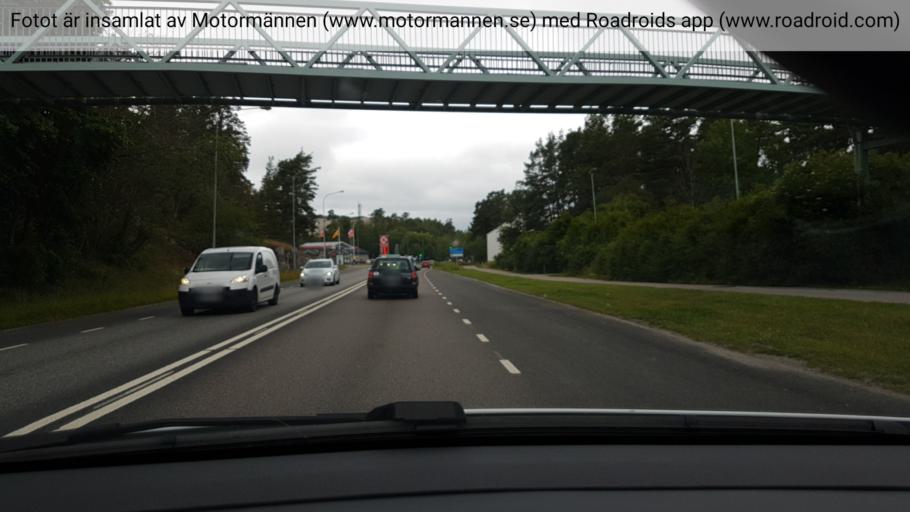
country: SE
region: Stockholm
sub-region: Vaxholms Kommun
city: Vaxholm
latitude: 59.4028
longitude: 18.3295
